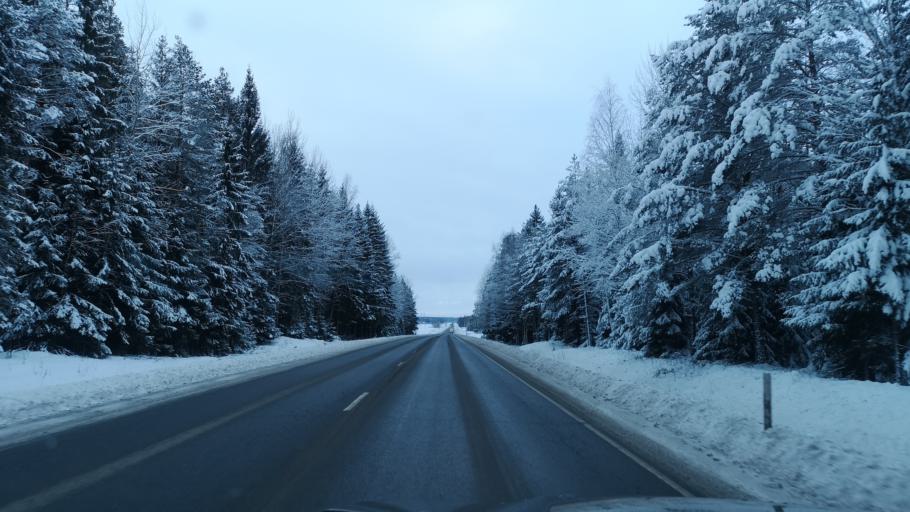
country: FI
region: Varsinais-Suomi
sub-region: Loimaa
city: Loimaa
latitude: 60.8996
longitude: 23.1343
